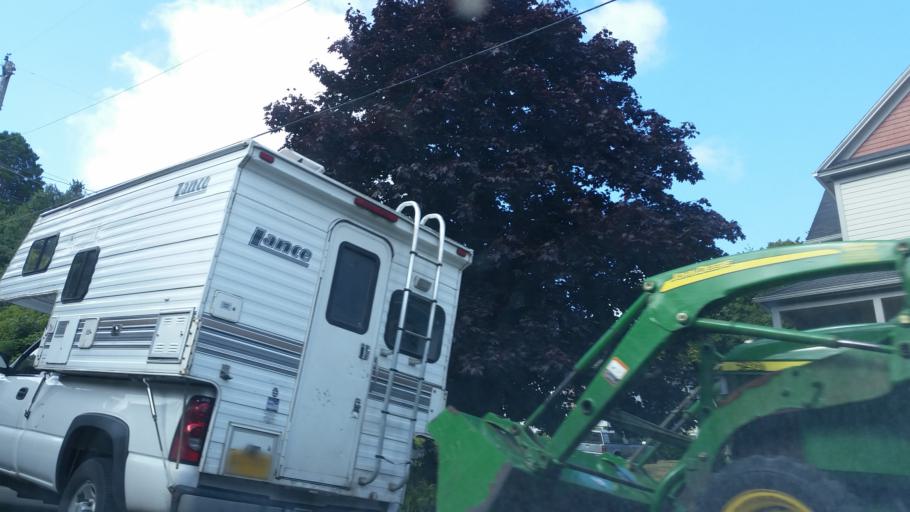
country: US
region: Oregon
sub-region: Clatsop County
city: Astoria
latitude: 46.1906
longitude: -123.8000
